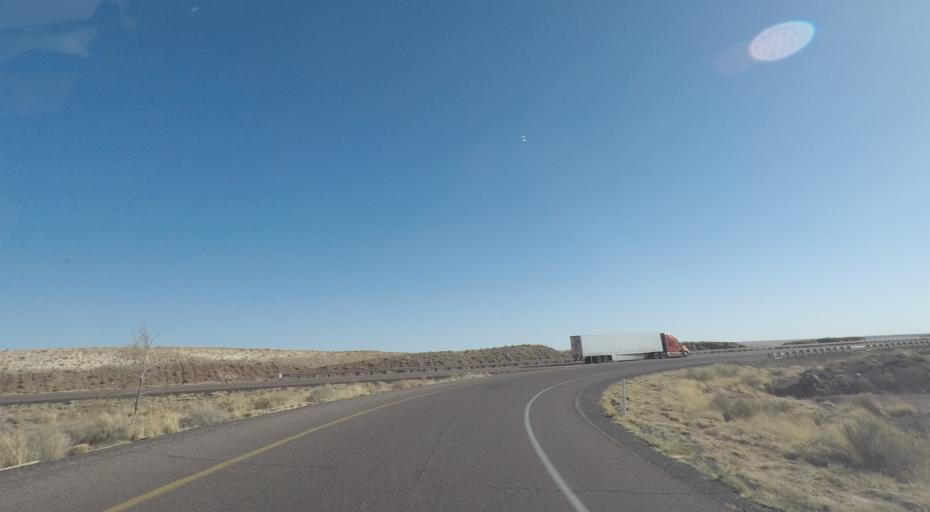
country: US
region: Arizona
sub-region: Navajo County
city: Holbrook
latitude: 34.9140
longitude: -110.1544
